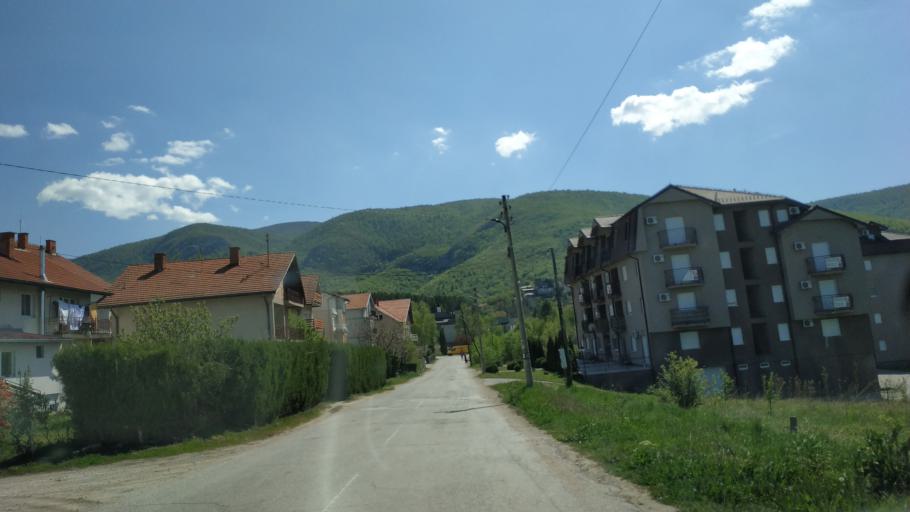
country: RS
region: Central Serbia
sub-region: Zajecarski Okrug
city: Soko Banja
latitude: 43.6472
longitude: 21.8820
